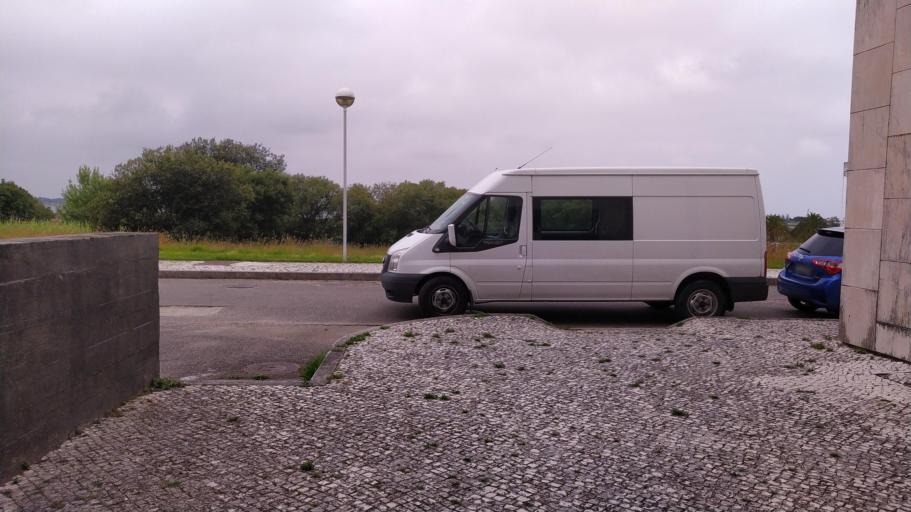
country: PT
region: Aveiro
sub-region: Aveiro
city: Aveiro
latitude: 40.6327
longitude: -8.6596
